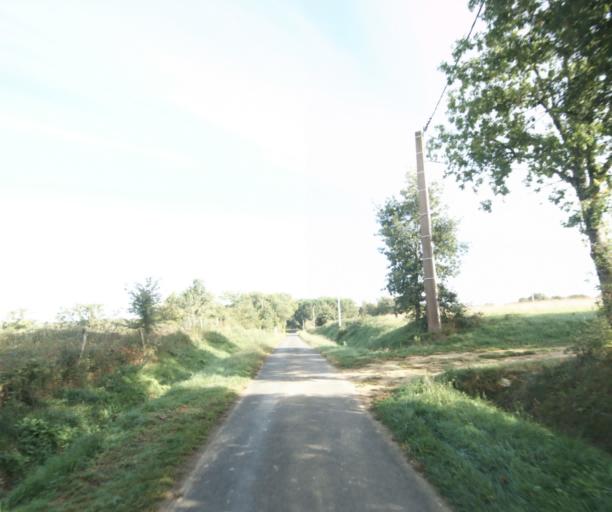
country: FR
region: Midi-Pyrenees
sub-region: Departement du Gers
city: Eauze
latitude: 43.8927
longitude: 0.1326
